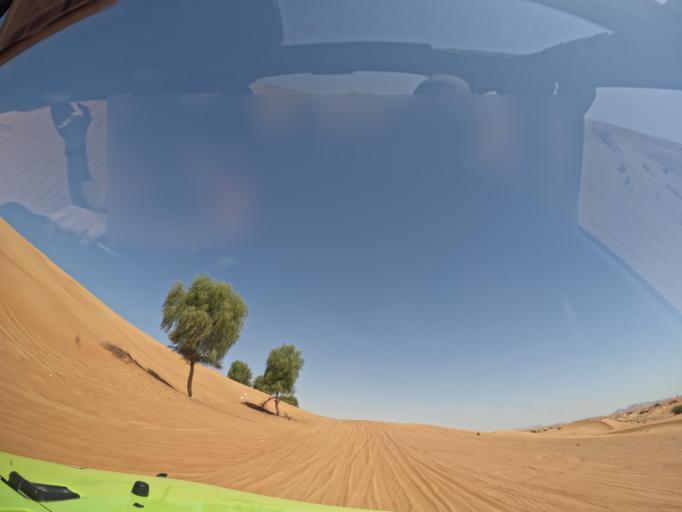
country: AE
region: Ash Shariqah
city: Adh Dhayd
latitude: 24.9741
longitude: 55.7212
